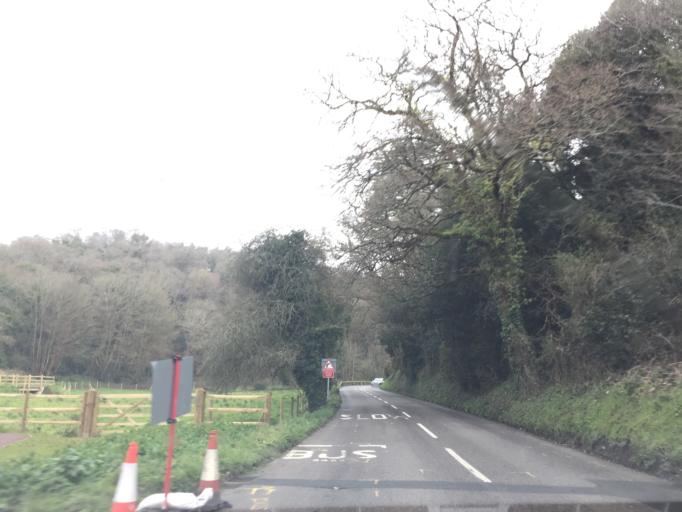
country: JE
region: St Helier
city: Saint Helier
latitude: 49.2087
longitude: -2.1608
